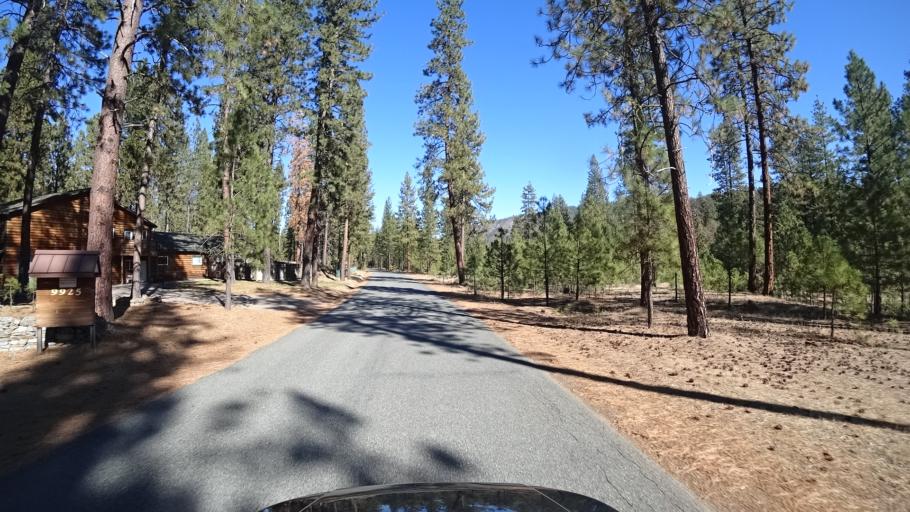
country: US
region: California
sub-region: Siskiyou County
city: Yreka
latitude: 41.5821
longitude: -122.9141
